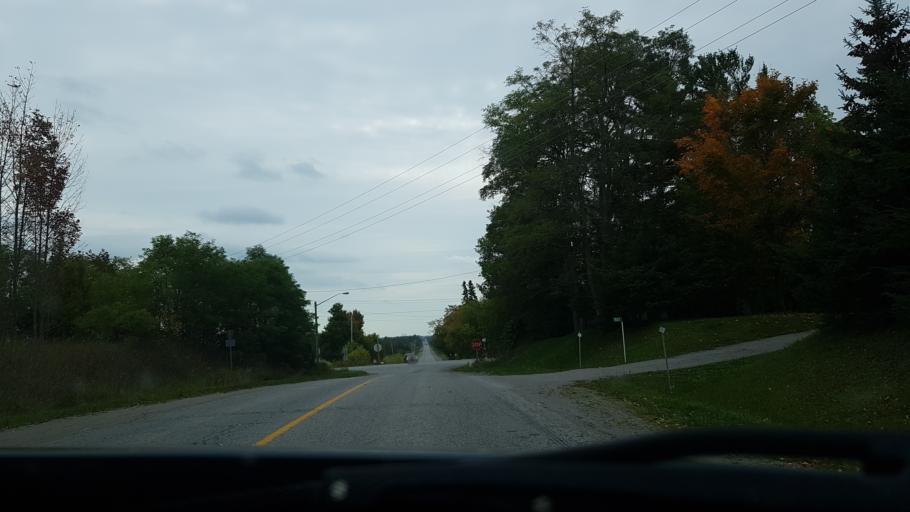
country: CA
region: Ontario
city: Omemee
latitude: 44.5808
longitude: -78.9321
